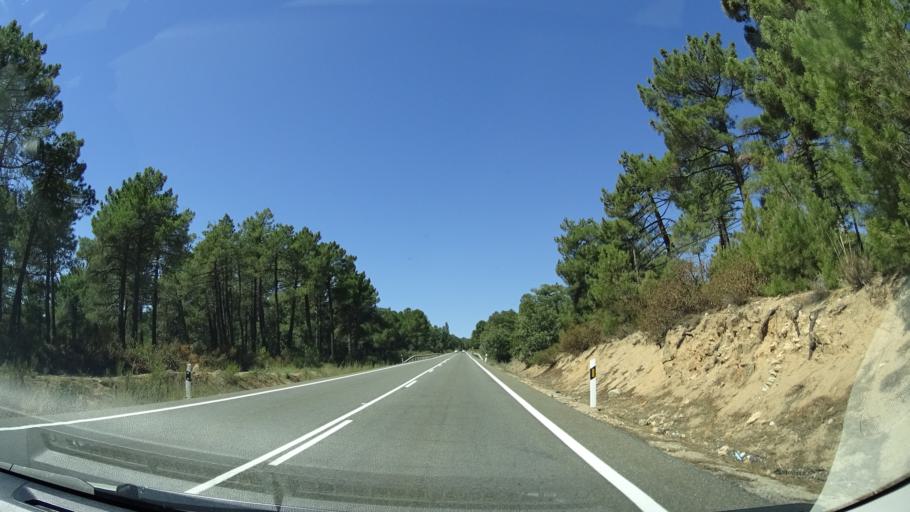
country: ES
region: Castille and Leon
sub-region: Provincia de Avila
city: Las Navas del Marques
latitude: 40.5925
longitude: -4.3707
